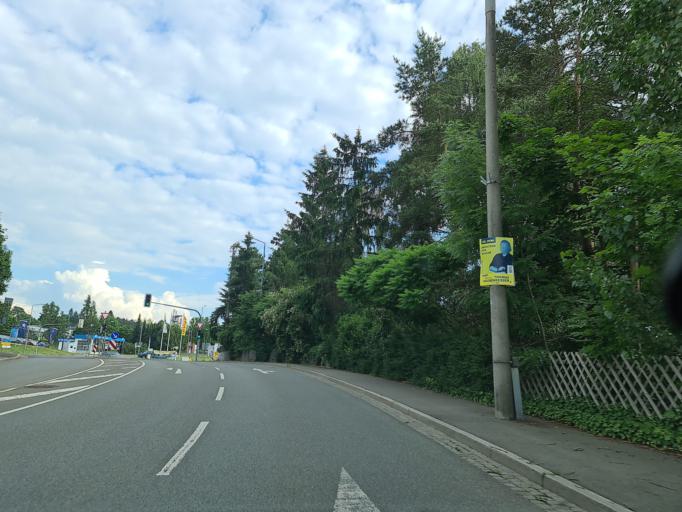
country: DE
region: Saxony
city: Plauen
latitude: 50.5094
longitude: 12.1582
